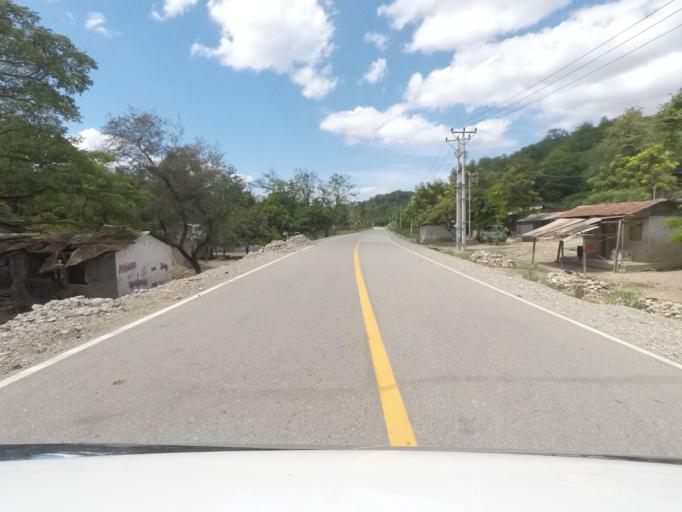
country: TL
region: Lautem
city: Lospalos
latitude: -8.4116
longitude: 126.7394
